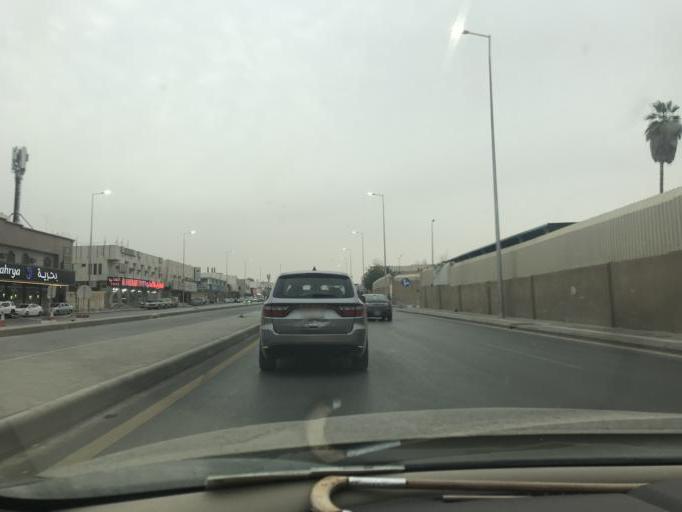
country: SA
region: Ar Riyad
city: Riyadh
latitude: 24.7571
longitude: 46.7671
